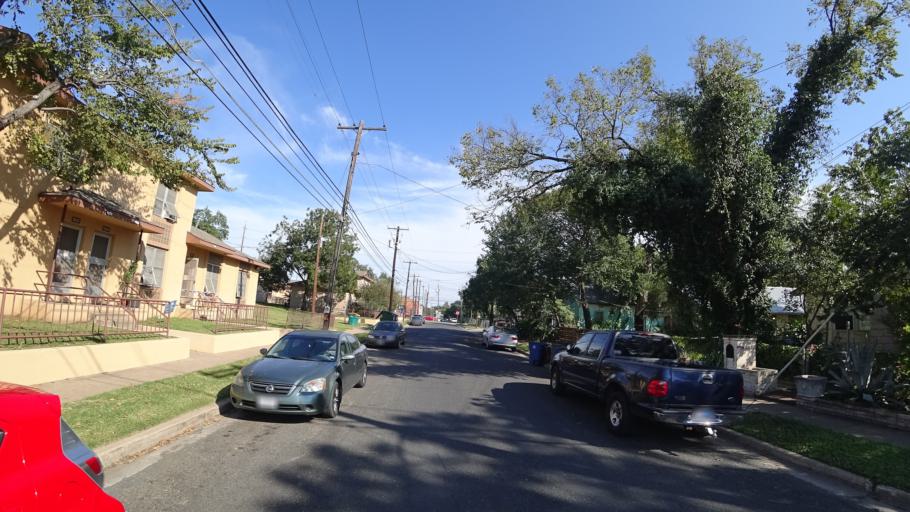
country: US
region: Texas
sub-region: Travis County
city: Austin
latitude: 30.2593
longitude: -97.7248
